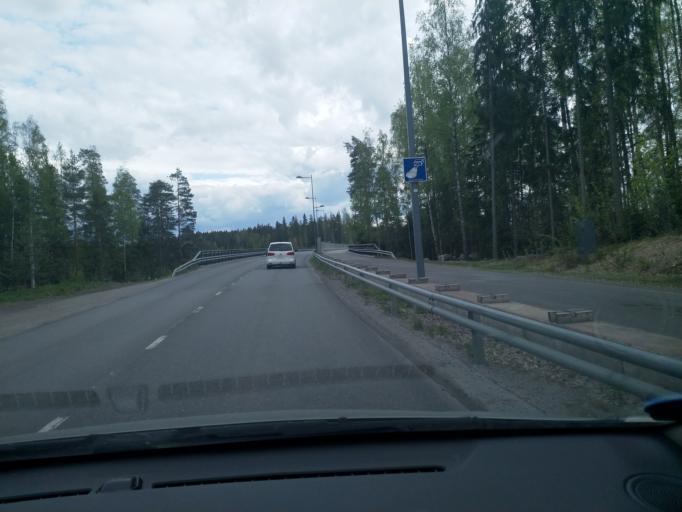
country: FI
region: Pirkanmaa
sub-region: Tampere
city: Tampere
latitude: 61.4508
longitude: 23.8037
